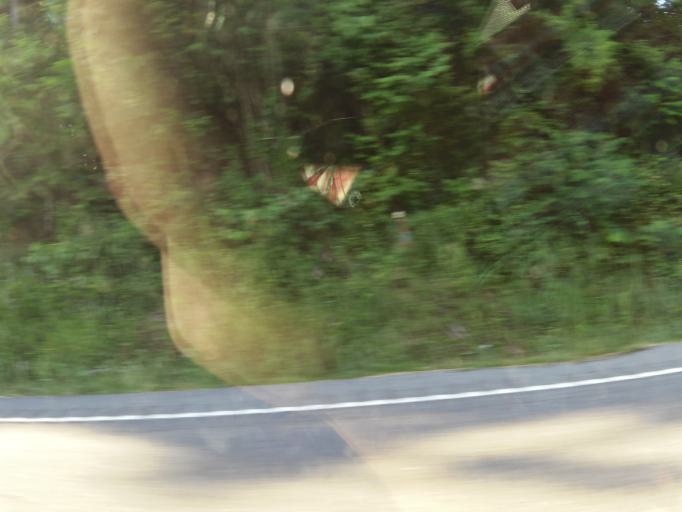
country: US
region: Tennessee
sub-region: Sevier County
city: Seymour
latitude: 35.8579
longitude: -83.6494
